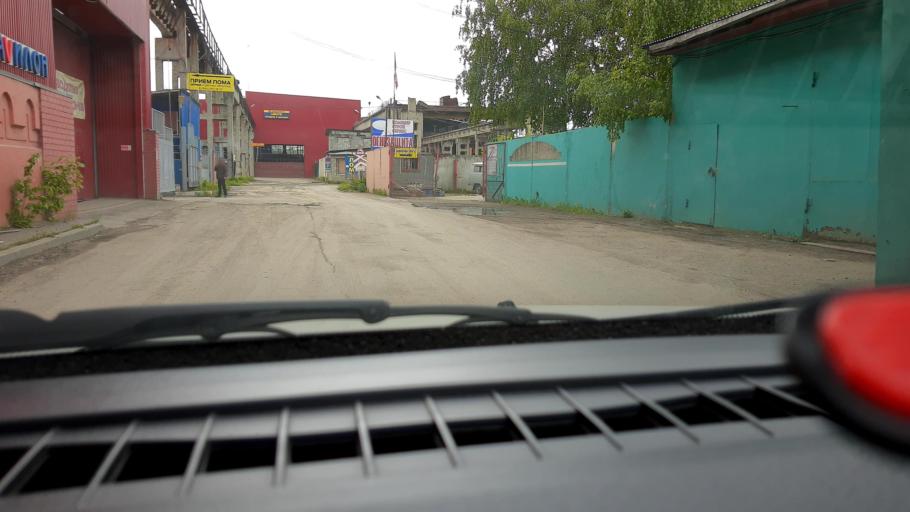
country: RU
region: Nizjnij Novgorod
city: Nizhniy Novgorod
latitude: 56.2626
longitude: 43.9224
